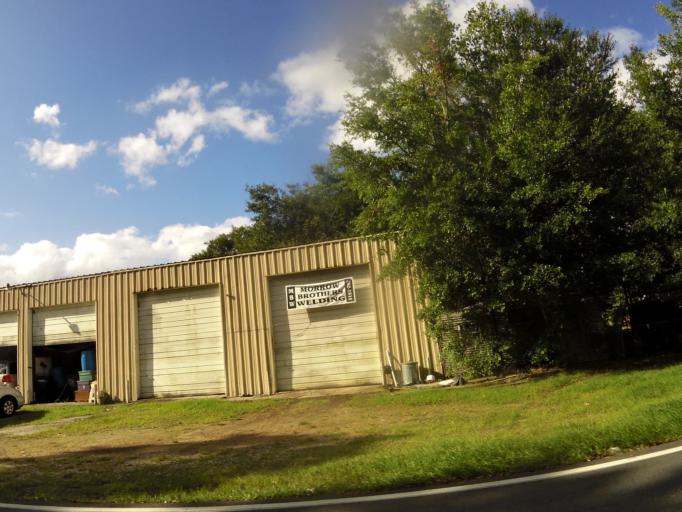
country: US
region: Florida
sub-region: Duval County
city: Jacksonville
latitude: 30.2813
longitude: -81.7385
